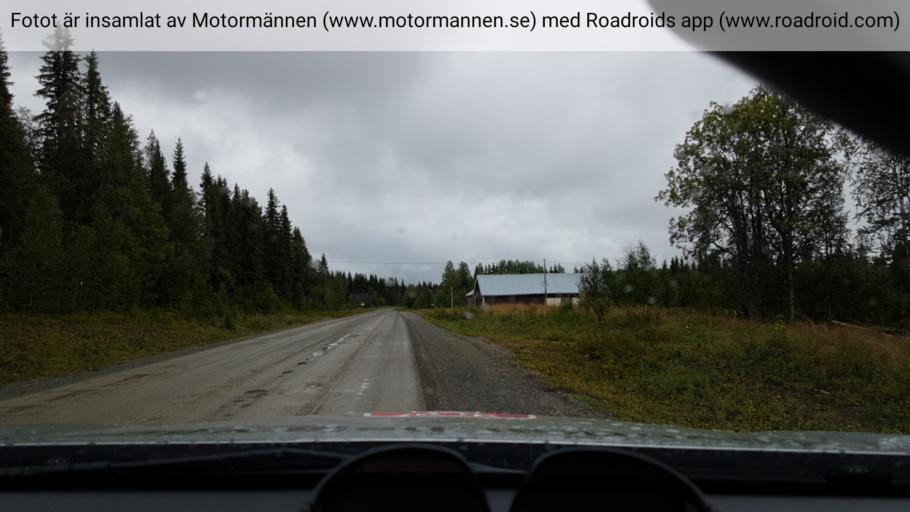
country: SE
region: Vaesterbotten
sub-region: Storumans Kommun
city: Storuman
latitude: 64.8562
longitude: 17.3911
